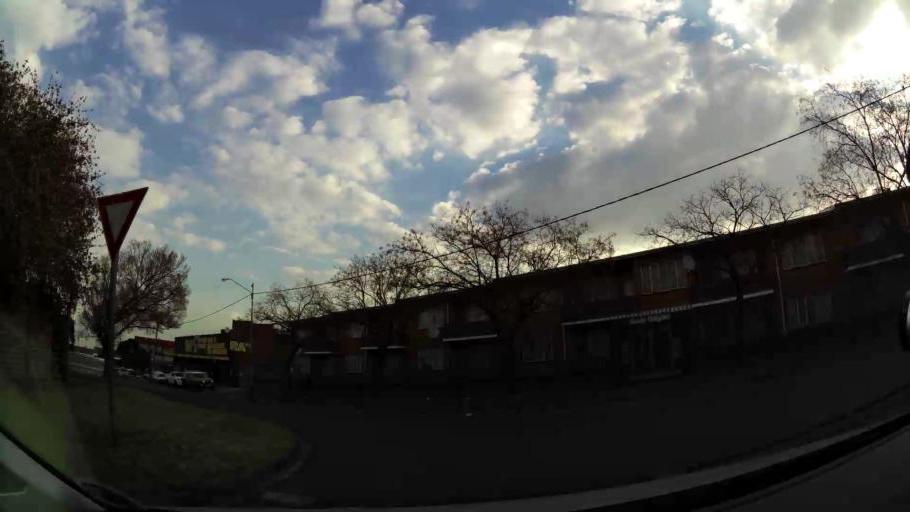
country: ZA
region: Gauteng
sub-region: Ekurhuleni Metropolitan Municipality
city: Germiston
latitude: -26.1711
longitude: 28.1772
